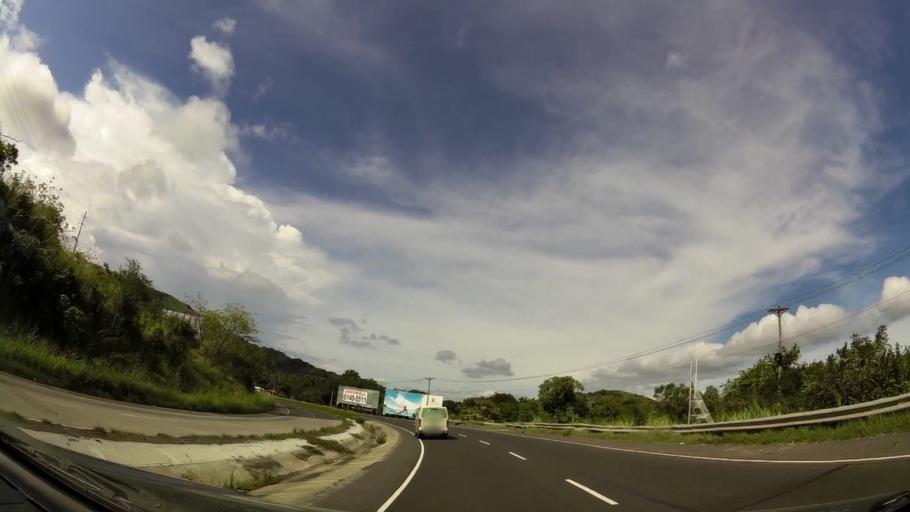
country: PA
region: Panama
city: Bejuco
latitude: 8.6564
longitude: -79.8710
